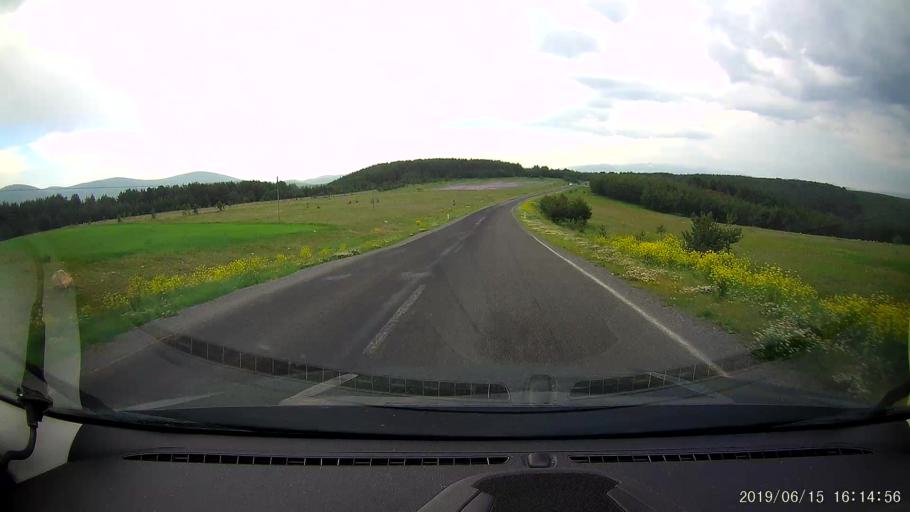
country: TR
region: Ardahan
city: Hanak
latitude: 41.2740
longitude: 42.8509
